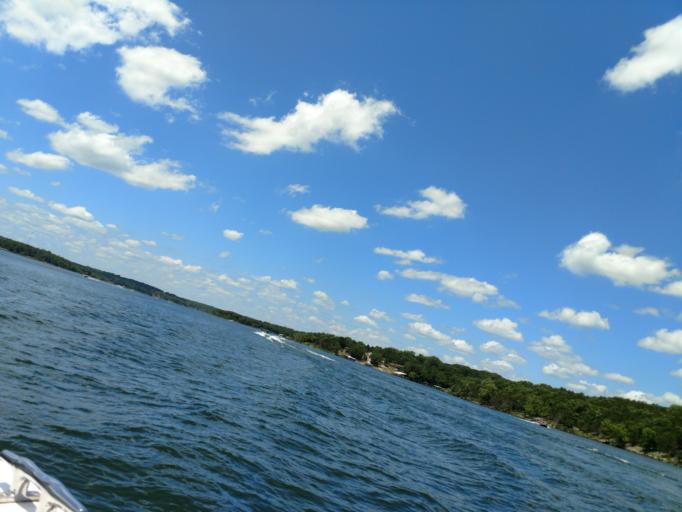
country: US
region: Missouri
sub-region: Barry County
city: Shell Knob
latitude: 36.5902
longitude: -93.5499
